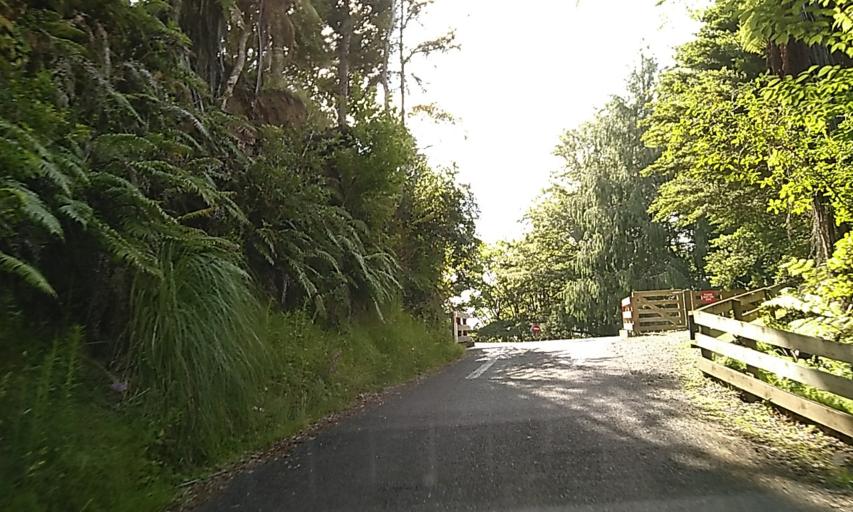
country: NZ
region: Bay of Plenty
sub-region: Tauranga City
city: Tauranga
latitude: -37.8136
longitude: 176.0448
